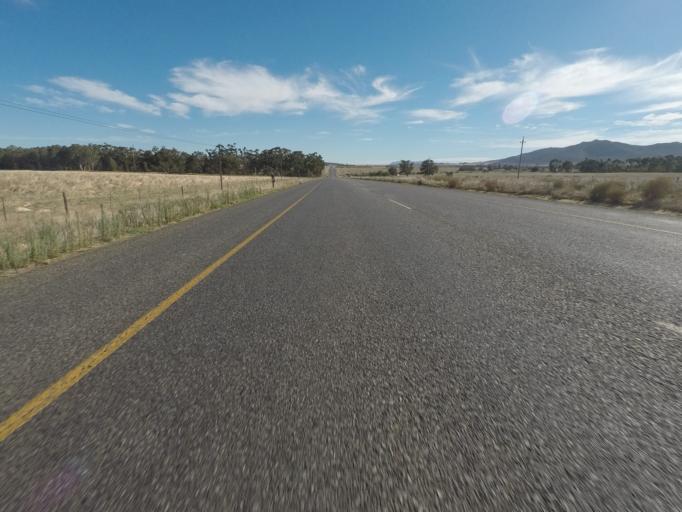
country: ZA
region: Western Cape
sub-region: West Coast District Municipality
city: Malmesbury
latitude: -33.6188
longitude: 18.7264
